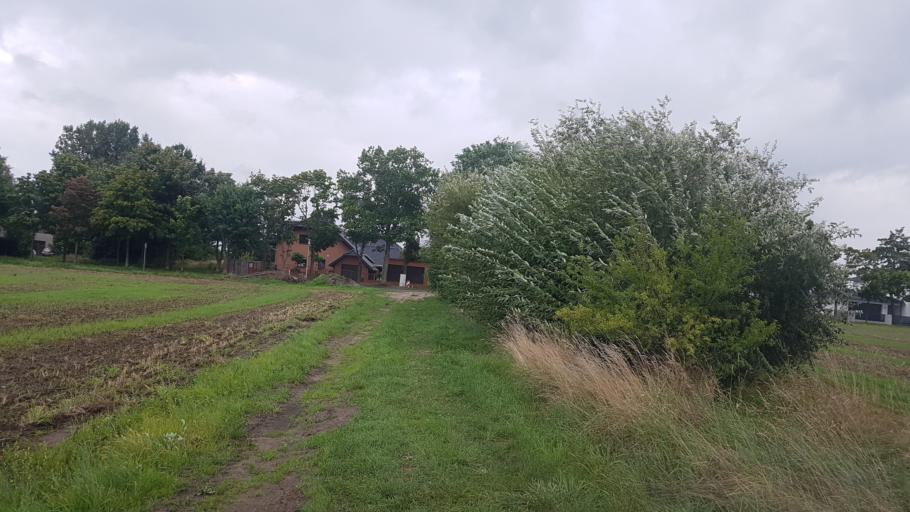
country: DE
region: Brandenburg
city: Doberlug-Kirchhain
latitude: 51.6378
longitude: 13.5430
